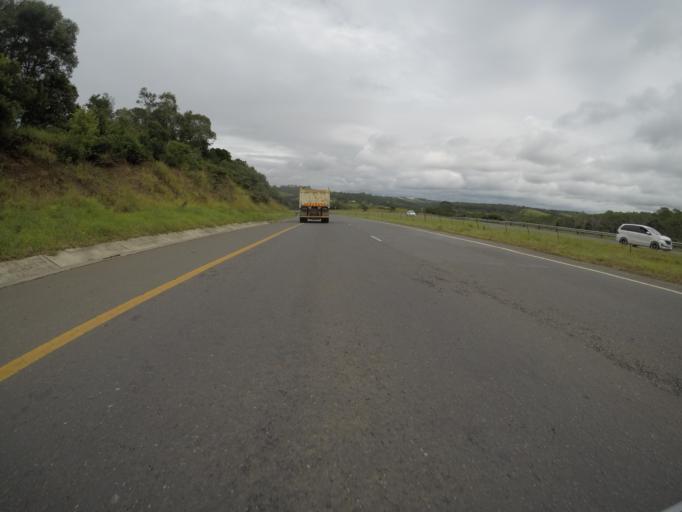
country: ZA
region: Eastern Cape
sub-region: Buffalo City Metropolitan Municipality
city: East London
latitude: -32.9409
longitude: 27.9460
